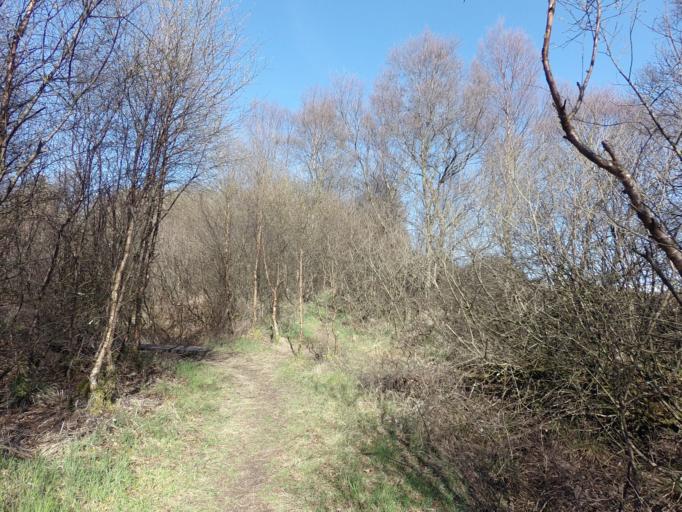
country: GB
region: Scotland
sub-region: West Lothian
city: West Calder
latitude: 55.8943
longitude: -3.5824
